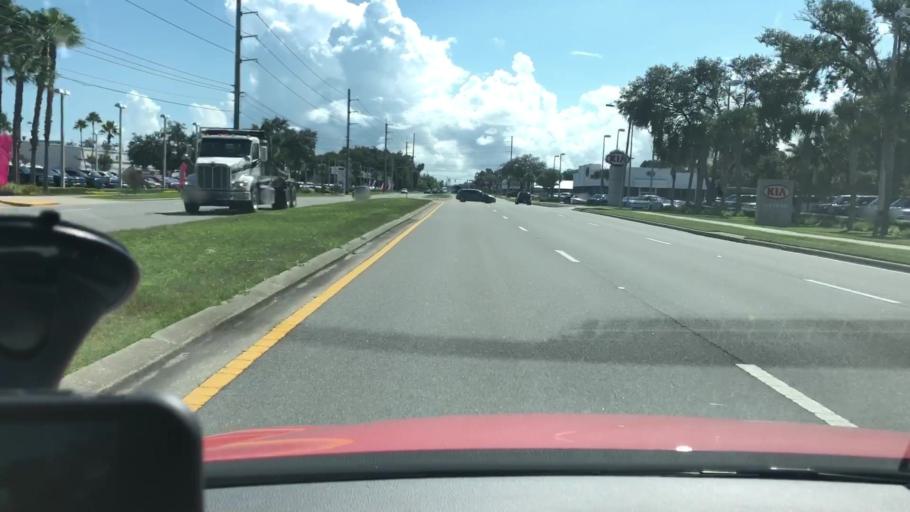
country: US
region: Florida
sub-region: Volusia County
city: Daytona Beach
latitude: 29.2140
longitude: -81.0455
